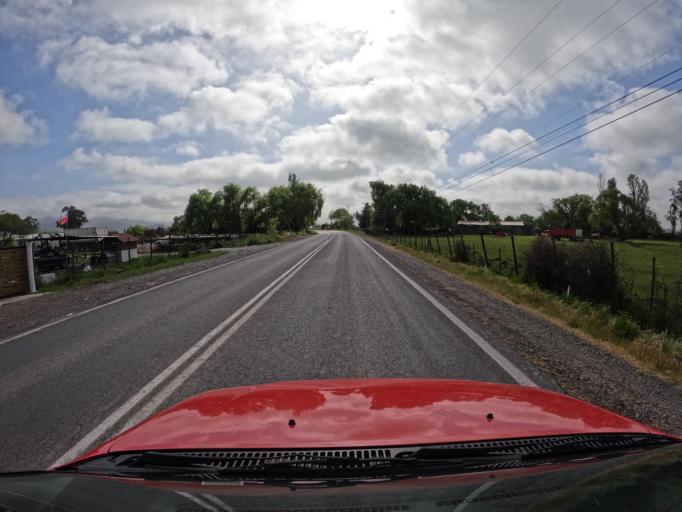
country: CL
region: Maule
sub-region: Provincia de Curico
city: Teno
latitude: -34.8488
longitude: -71.1912
